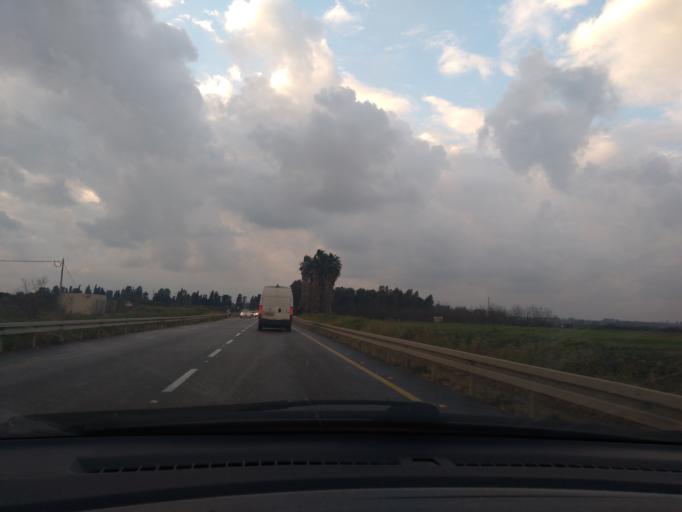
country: IL
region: Central District
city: Elyakhin
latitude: 32.3755
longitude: 34.9009
